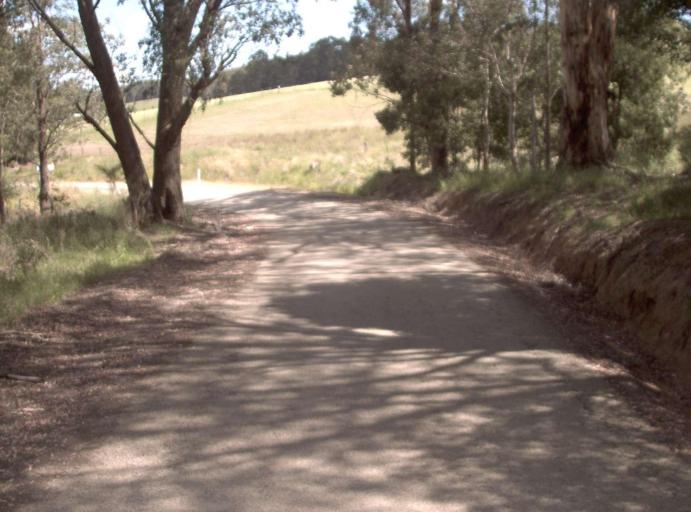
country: AU
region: New South Wales
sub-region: Bombala
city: Bombala
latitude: -37.1872
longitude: 148.7255
